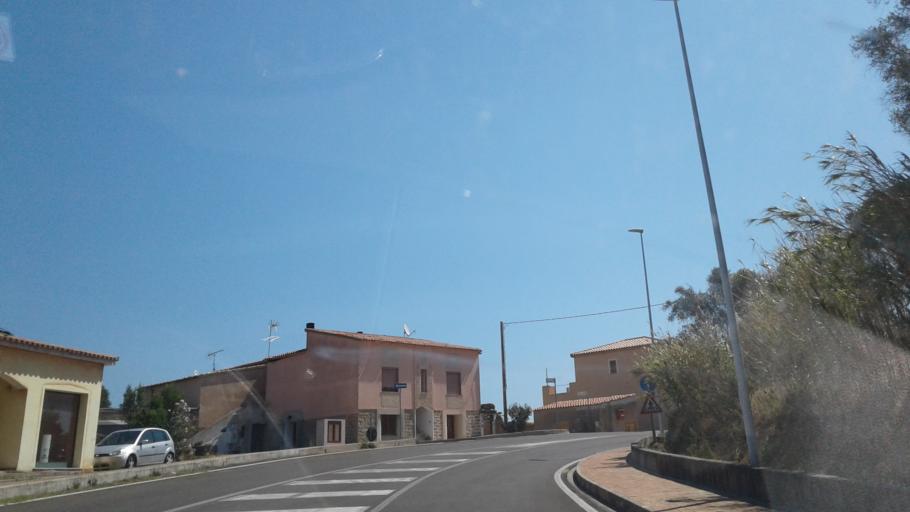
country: IT
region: Sardinia
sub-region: Provincia di Olbia-Tempio
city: Palau
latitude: 41.1704
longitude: 9.3205
